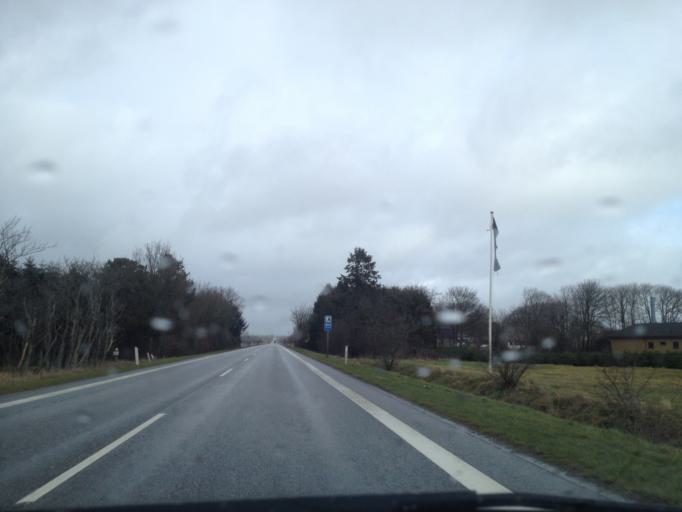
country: DK
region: South Denmark
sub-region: Tonder Kommune
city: Toftlund
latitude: 55.2328
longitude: 9.1214
